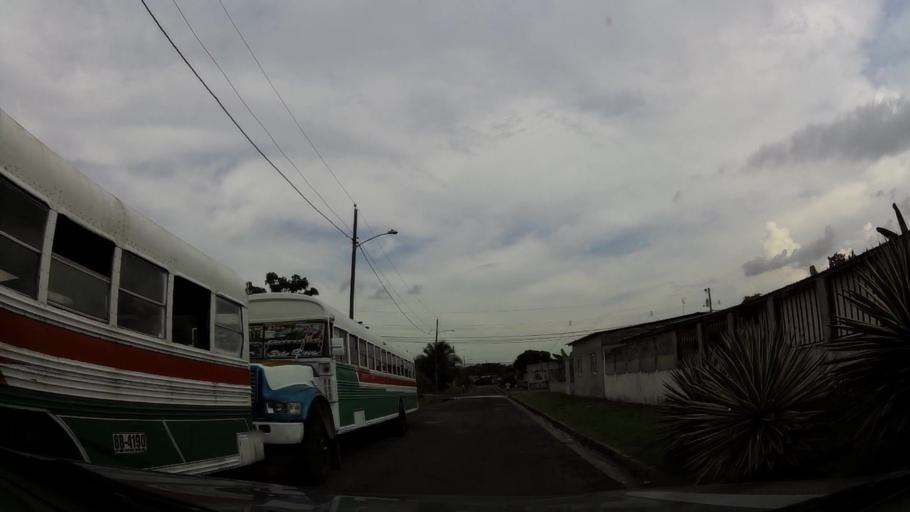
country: PA
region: Panama
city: Cabra Numero Uno
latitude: 9.0963
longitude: -79.3481
